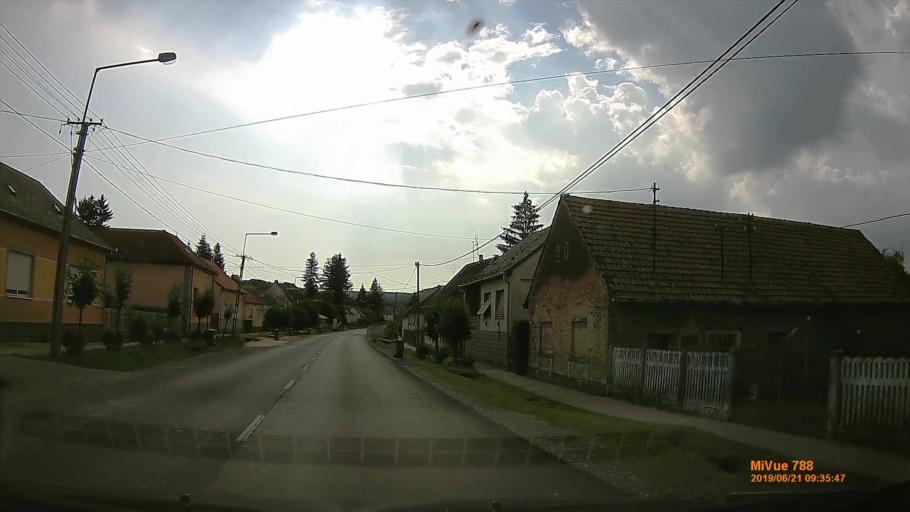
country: HU
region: Somogy
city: Taszar
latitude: 46.3188
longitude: 17.8965
